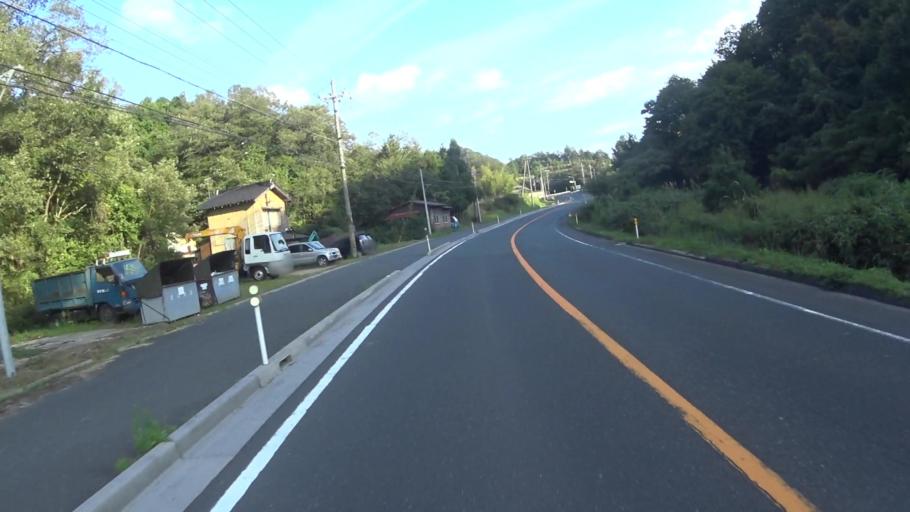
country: JP
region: Hyogo
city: Toyooka
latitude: 35.5859
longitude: 134.9520
